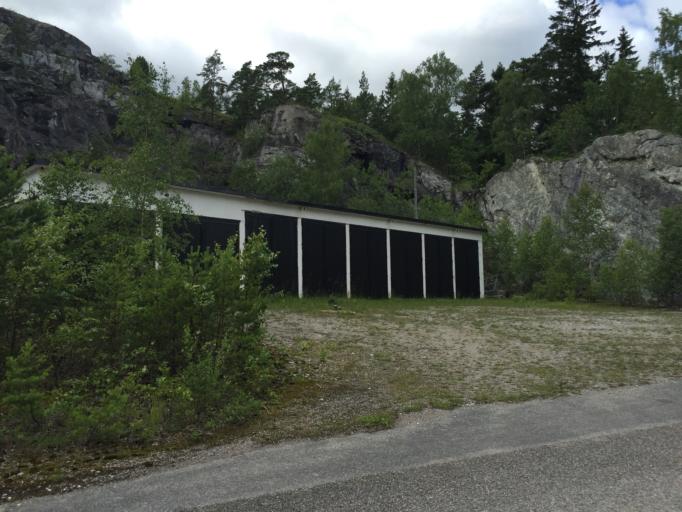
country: SE
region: Stockholm
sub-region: Nynashamns Kommun
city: Osmo
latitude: 58.9747
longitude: 17.7161
